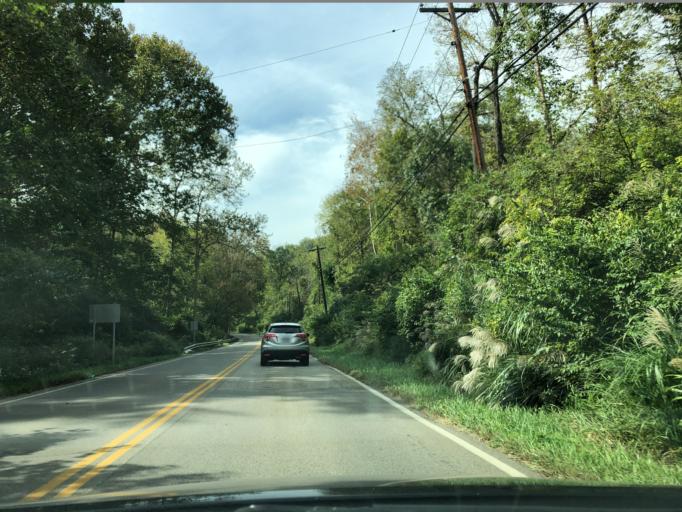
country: US
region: Ohio
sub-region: Clermont County
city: Milford
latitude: 39.1790
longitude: -84.2956
